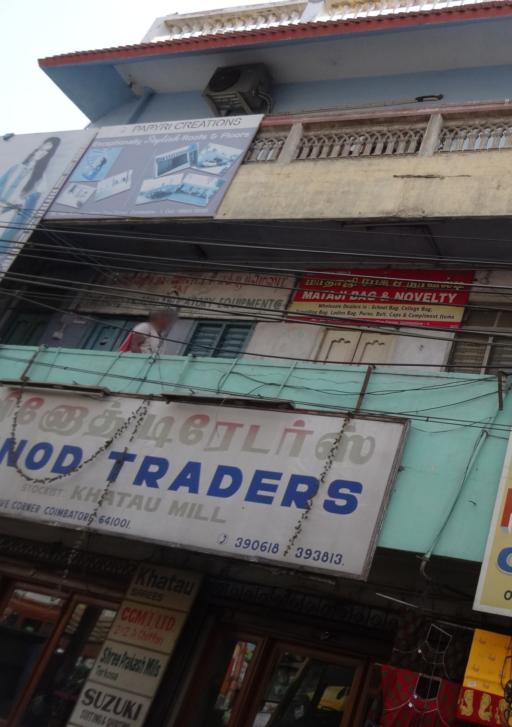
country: IN
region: Tamil Nadu
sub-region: Coimbatore
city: Coimbatore
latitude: 10.9953
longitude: 76.9605
